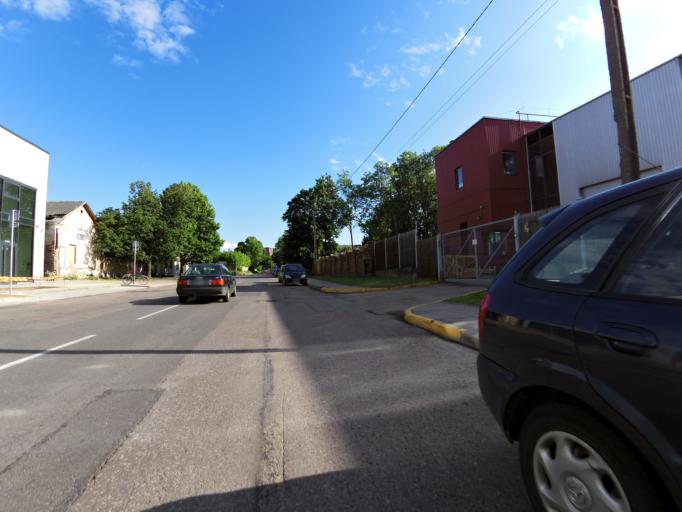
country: LT
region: Vilnius County
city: Naujamiestis
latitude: 54.6696
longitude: 25.2738
